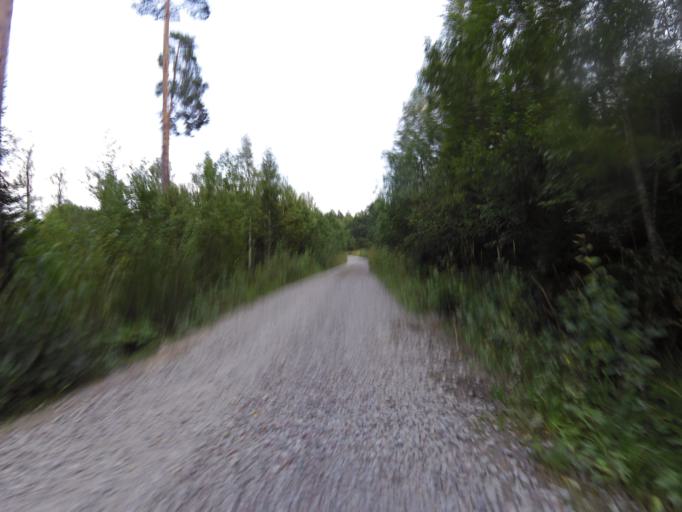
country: SE
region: Gaevleborg
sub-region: Gavle Kommun
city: Gavle
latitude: 60.7064
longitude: 17.1289
